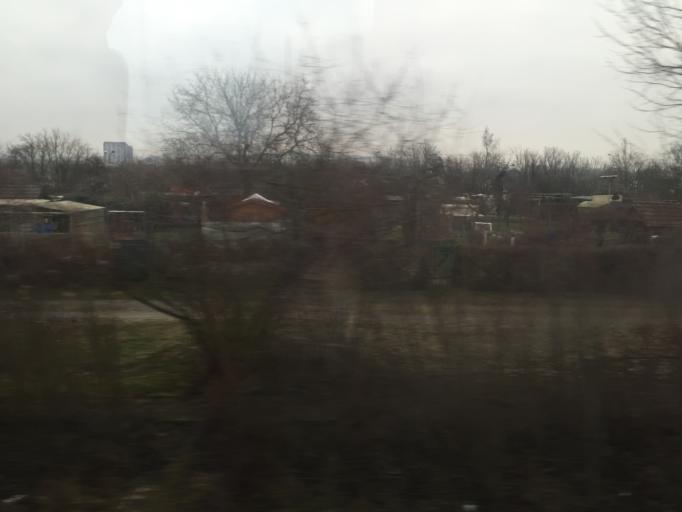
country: DE
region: Baden-Wuerttemberg
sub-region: Regierungsbezirk Stuttgart
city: Heilbronn
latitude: 49.1399
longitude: 9.1985
